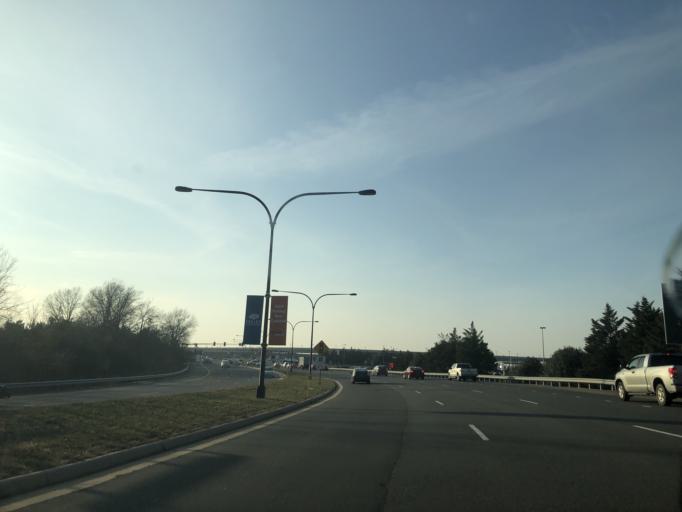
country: US
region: Virginia
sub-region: Fairfax County
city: Floris
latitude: 38.9643
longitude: -77.4444
